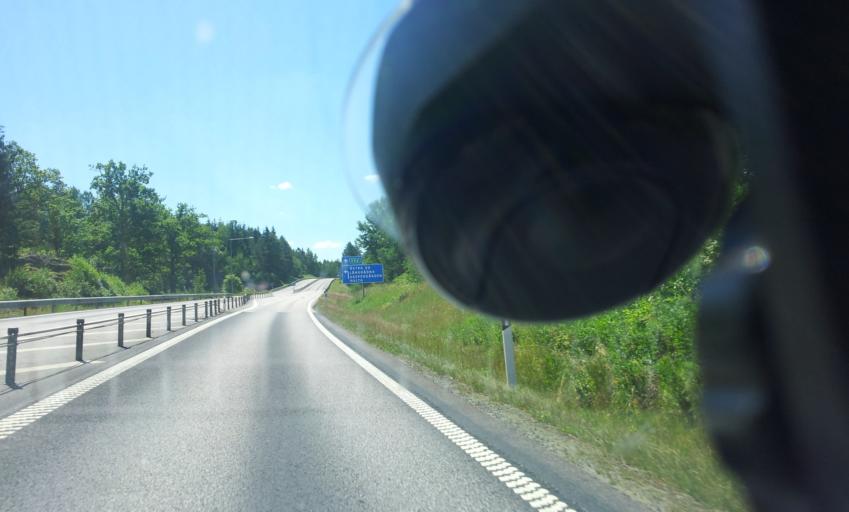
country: SE
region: Kalmar
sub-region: Vasterviks Kommun
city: Forserum
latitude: 58.0186
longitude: 16.5176
